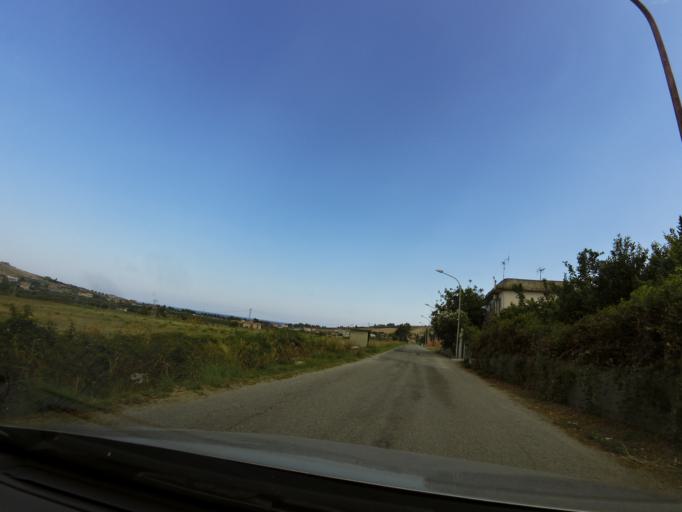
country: IT
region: Calabria
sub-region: Provincia di Reggio Calabria
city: Monasterace
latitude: 38.4250
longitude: 16.5374
